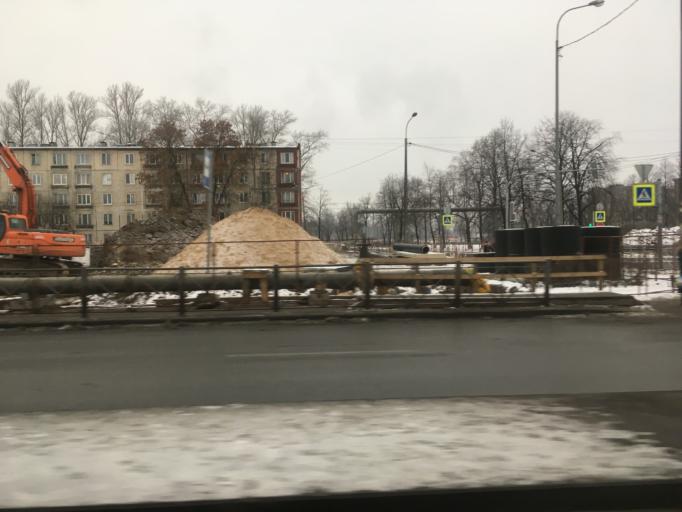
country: RU
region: St.-Petersburg
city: Obukhovo
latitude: 59.8704
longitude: 30.4403
